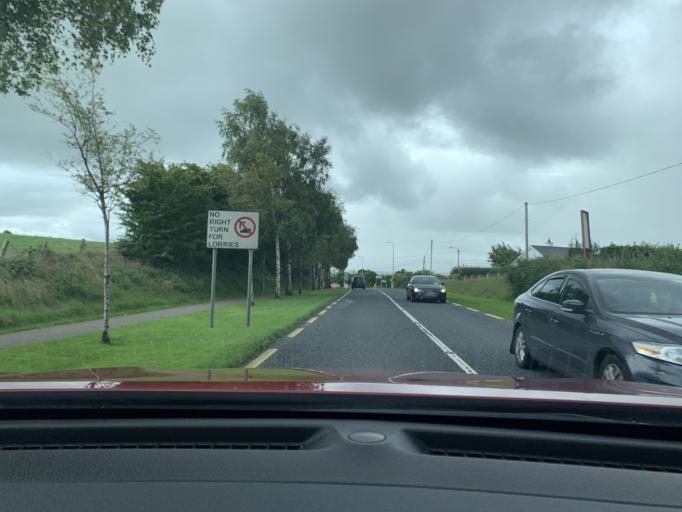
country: IE
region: Ulster
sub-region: County Donegal
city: Raphoe
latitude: 54.8015
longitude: -7.5829
